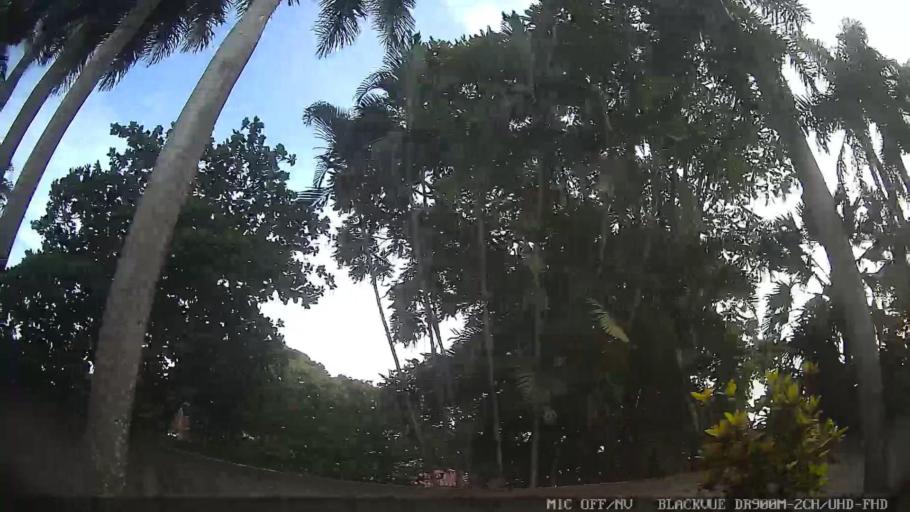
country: BR
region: Sao Paulo
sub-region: Jaguariuna
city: Jaguariuna
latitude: -22.6335
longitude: -47.0481
